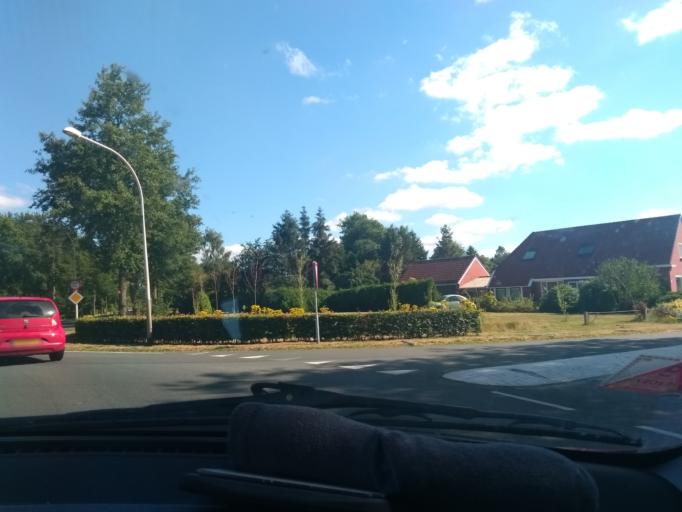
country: NL
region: Drenthe
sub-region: Gemeente Tynaarlo
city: Vries
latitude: 53.0977
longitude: 6.5465
